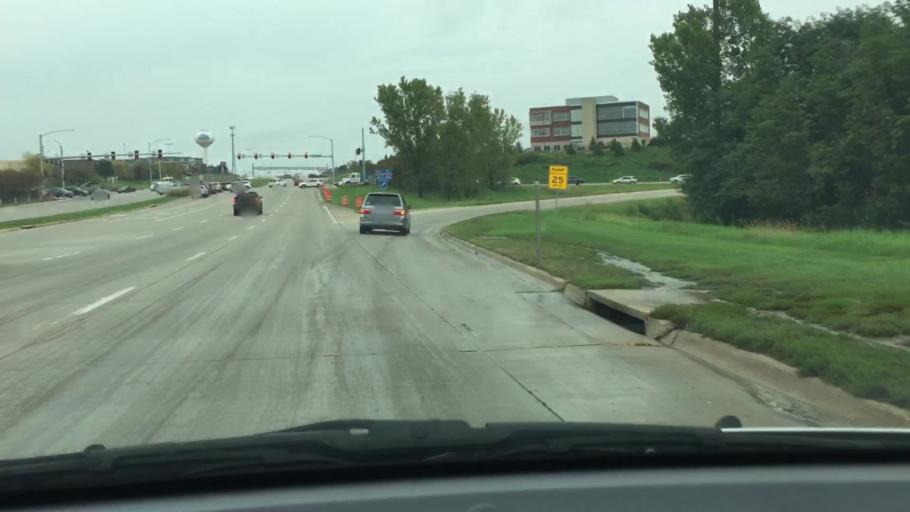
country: US
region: Iowa
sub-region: Johnson County
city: Coralville
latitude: 41.6943
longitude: -91.6083
